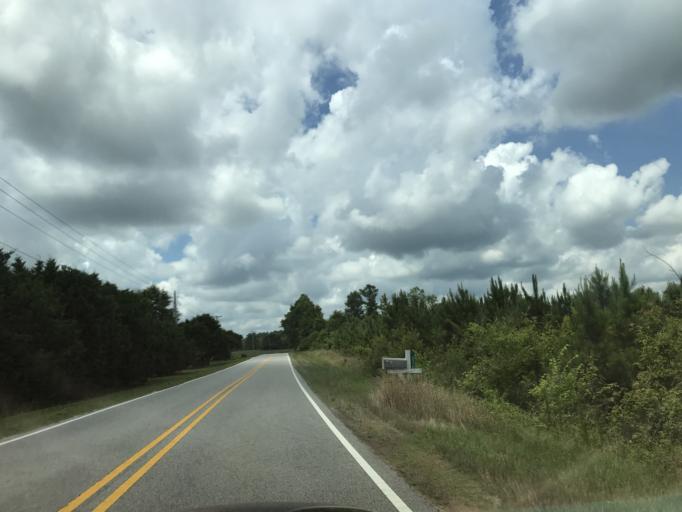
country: US
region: North Carolina
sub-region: Wake County
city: Rolesville
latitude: 35.9586
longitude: -78.3994
